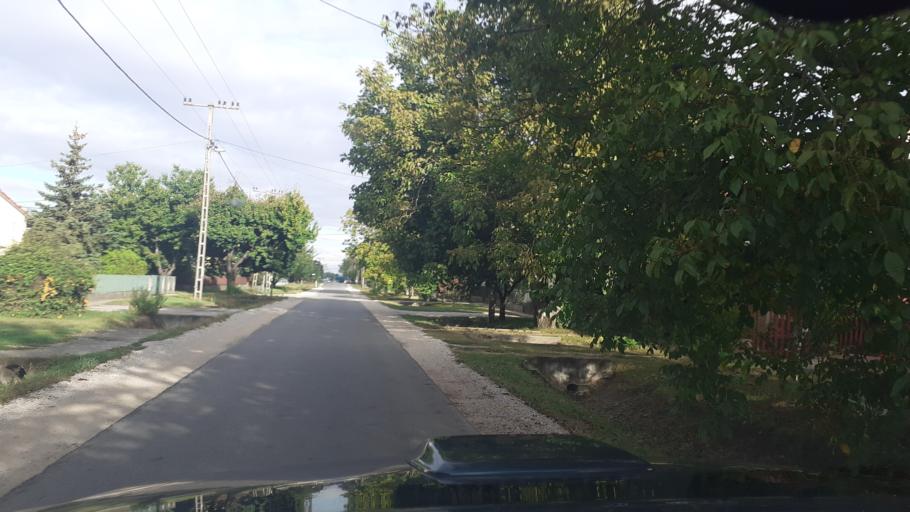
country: HU
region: Fejer
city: dunaujvaros
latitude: 46.9513
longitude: 18.8570
